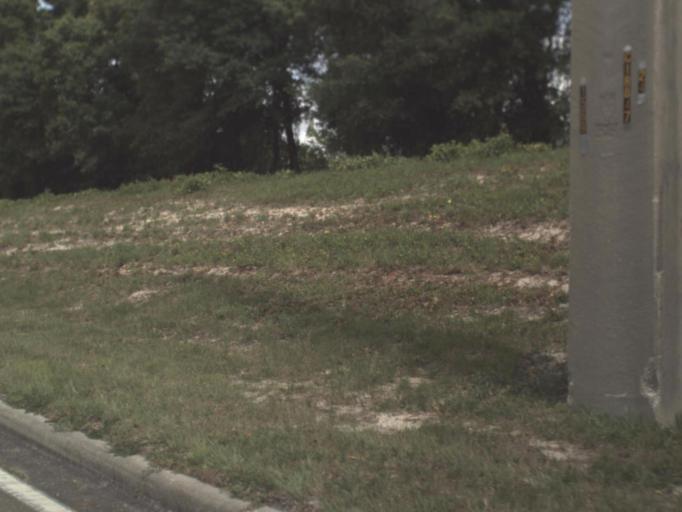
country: US
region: Florida
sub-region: Duval County
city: Jacksonville
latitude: 30.4137
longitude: -81.6169
